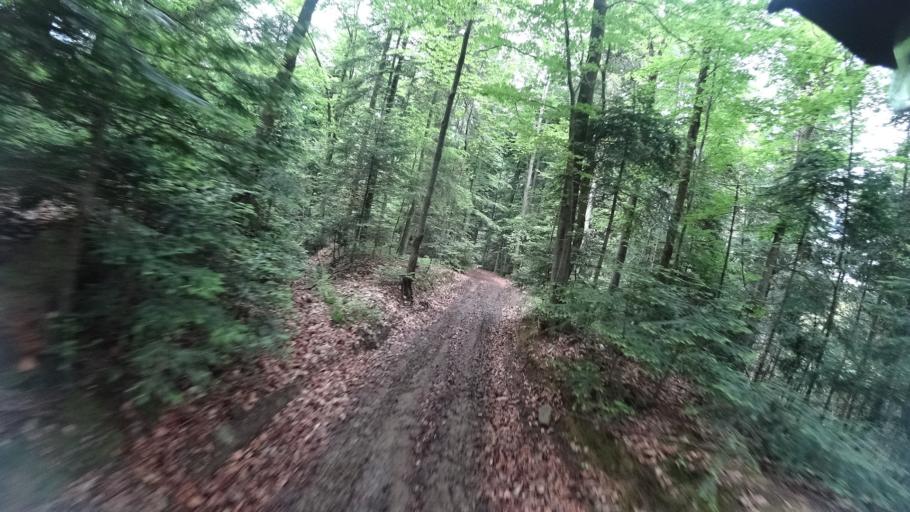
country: HR
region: Krapinsko-Zagorska
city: Oroslavje
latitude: 45.9423
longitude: 15.9432
